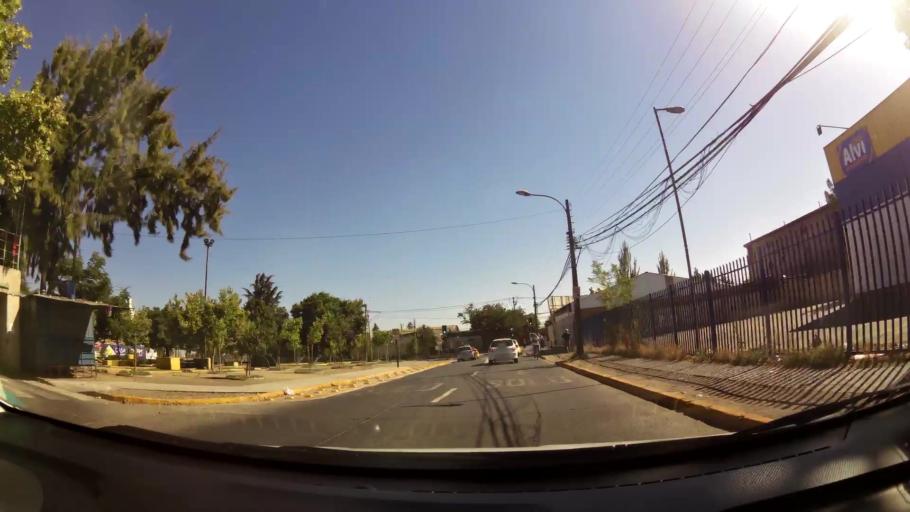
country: CL
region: O'Higgins
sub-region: Provincia de Cachapoal
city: Rancagua
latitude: -34.1645
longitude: -70.7504
